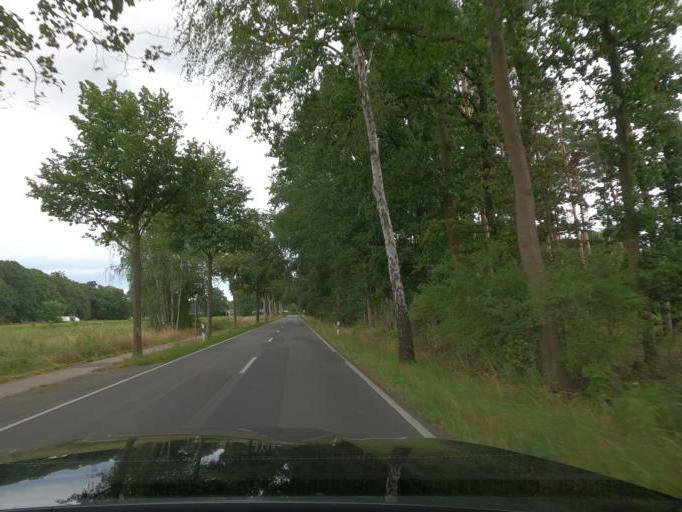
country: DE
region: Lower Saxony
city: Isernhagen Farster Bauerschaft
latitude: 52.4709
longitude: 9.8699
